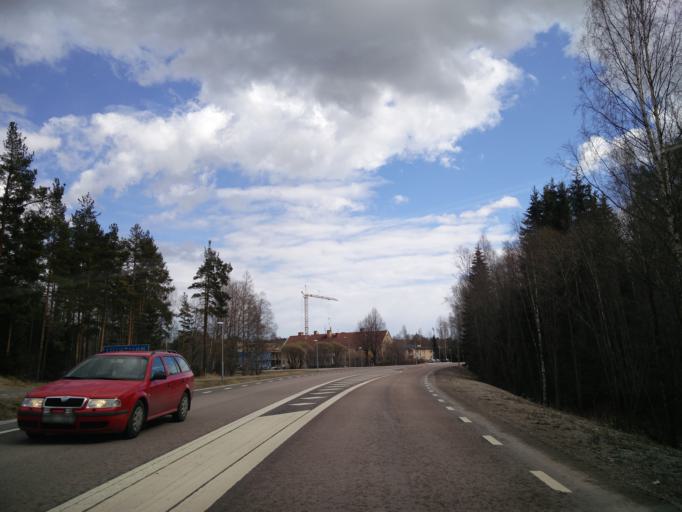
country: SE
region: Vaesternorrland
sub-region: Sundsvalls Kommun
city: Sundsvall
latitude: 62.4156
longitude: 17.2143
